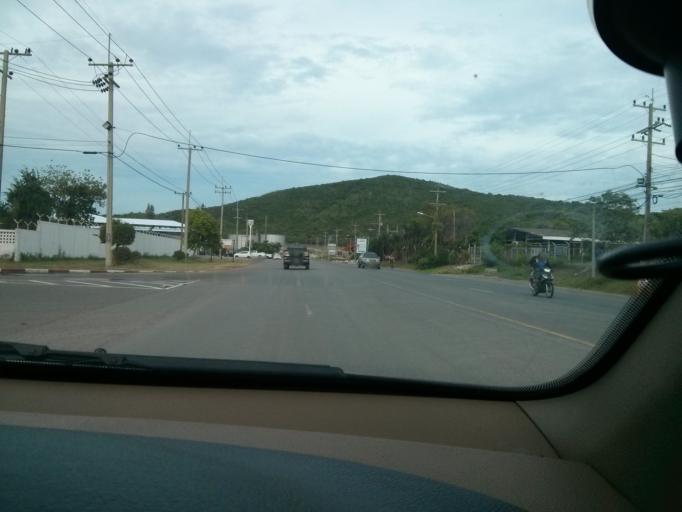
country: TH
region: Chon Buri
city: Sattahip
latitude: 12.6234
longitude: 100.9291
